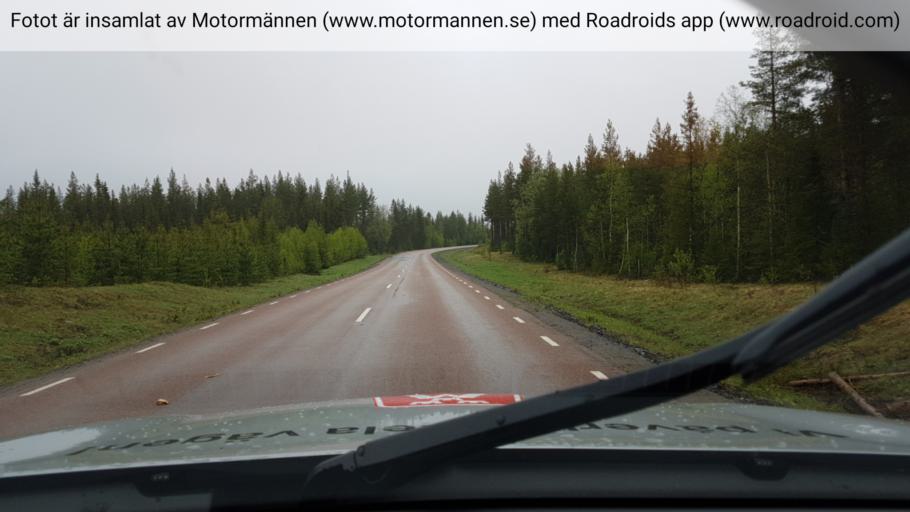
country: SE
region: Jaemtland
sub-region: Krokoms Kommun
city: Valla
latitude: 63.1758
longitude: 14.0043
